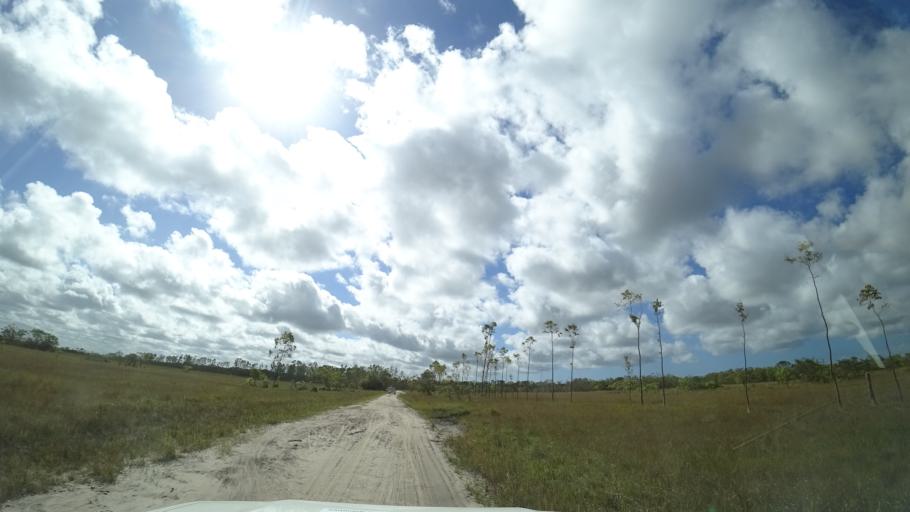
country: MZ
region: Sofala
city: Beira
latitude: -19.6116
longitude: 35.0788
